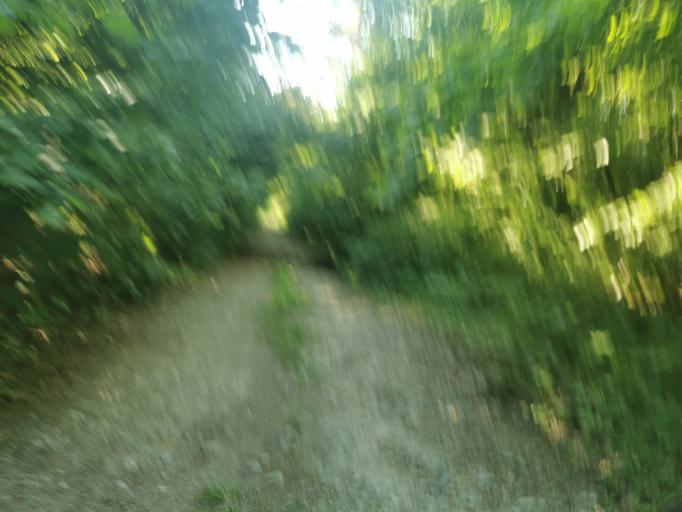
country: SK
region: Trnavsky
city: Smolenice
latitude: 48.5796
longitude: 17.4342
